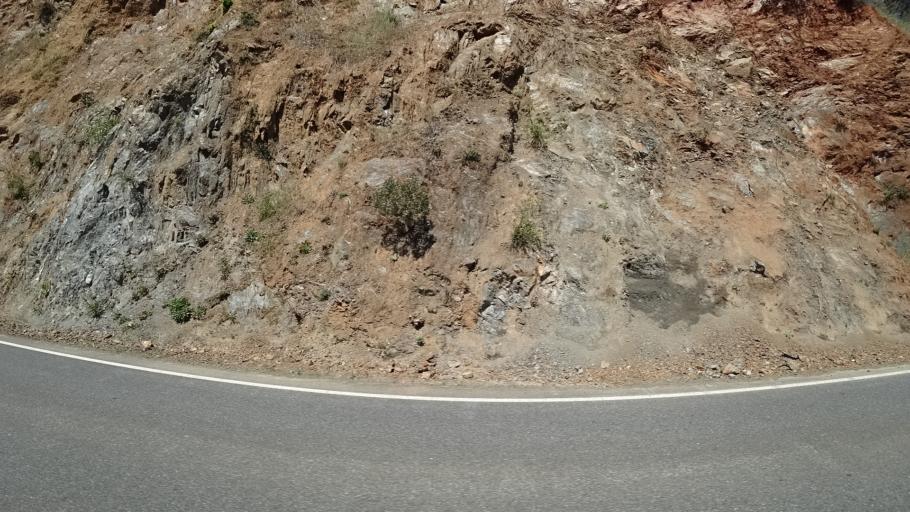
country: US
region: California
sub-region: Trinity County
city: Weaverville
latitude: 40.7646
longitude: -123.0766
